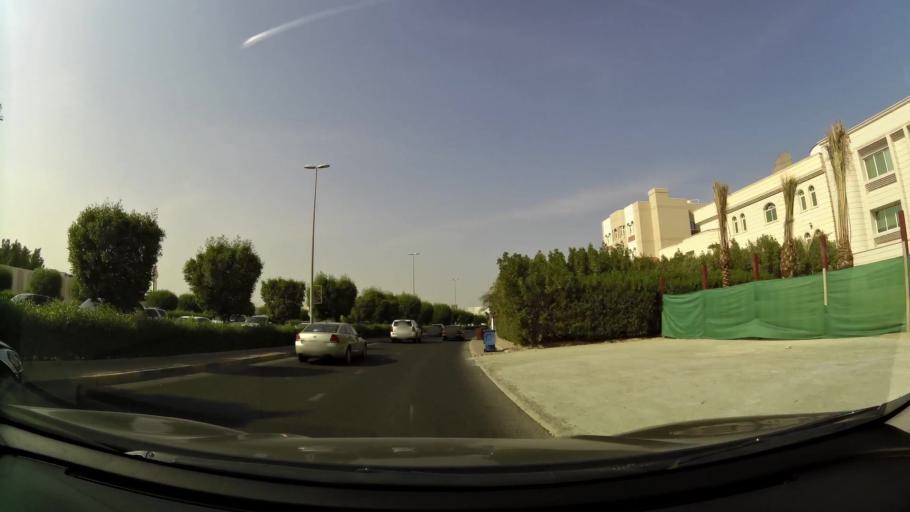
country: KW
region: Mubarak al Kabir
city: Mubarak al Kabir
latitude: 29.1851
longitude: 48.0808
